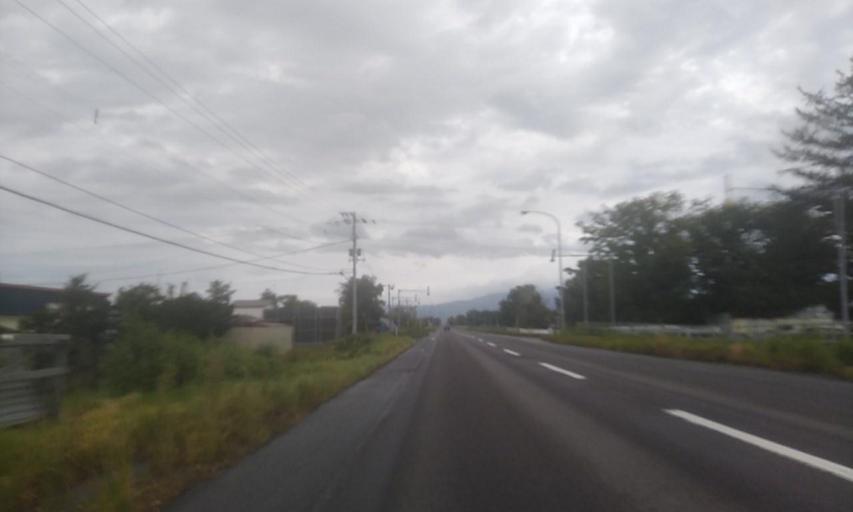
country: JP
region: Hokkaido
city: Abashiri
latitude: 43.8991
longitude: 144.6244
